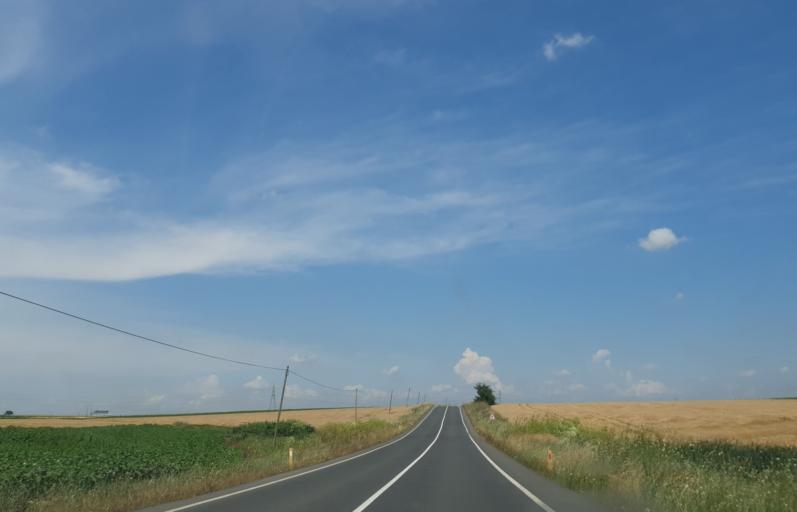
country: TR
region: Kirklareli
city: Buyukkaristiran
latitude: 41.2488
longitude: 27.6136
